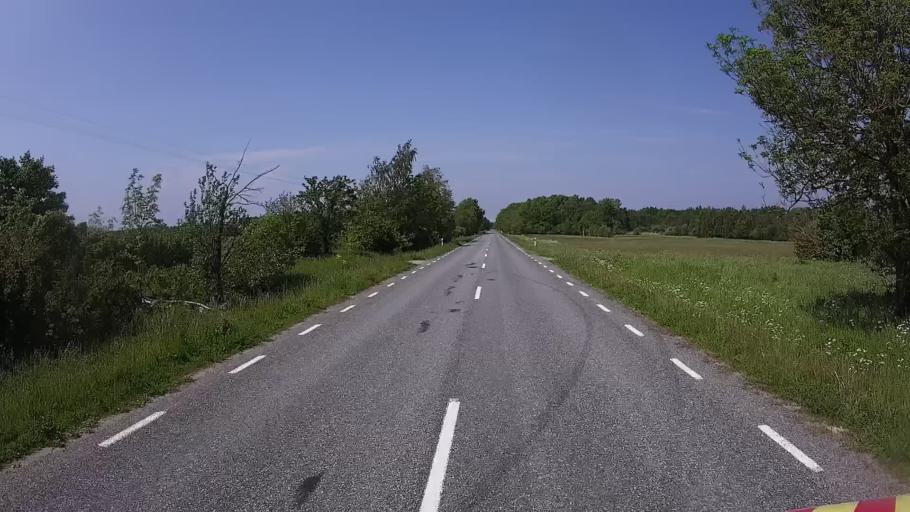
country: EE
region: Saare
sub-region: Kuressaare linn
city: Kuressaare
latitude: 58.3700
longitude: 22.0473
